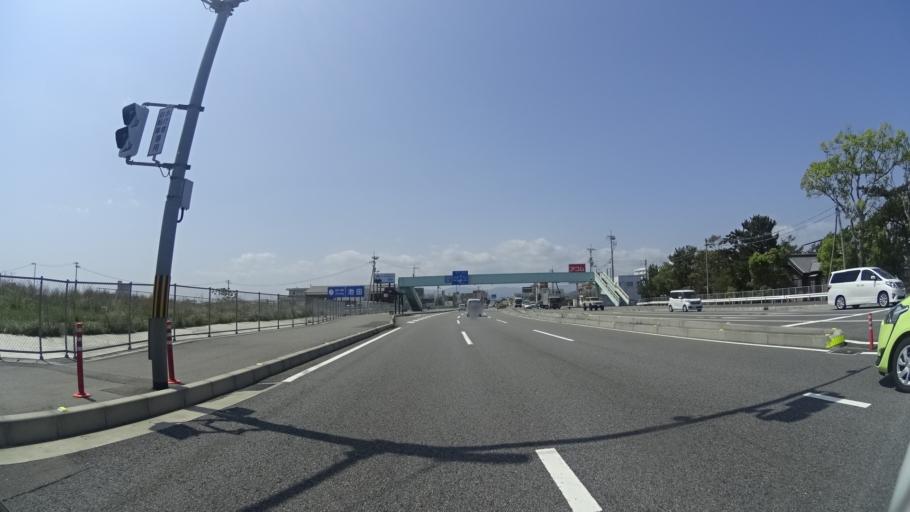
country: JP
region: Tokushima
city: Tokushima-shi
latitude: 34.1003
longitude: 134.5752
